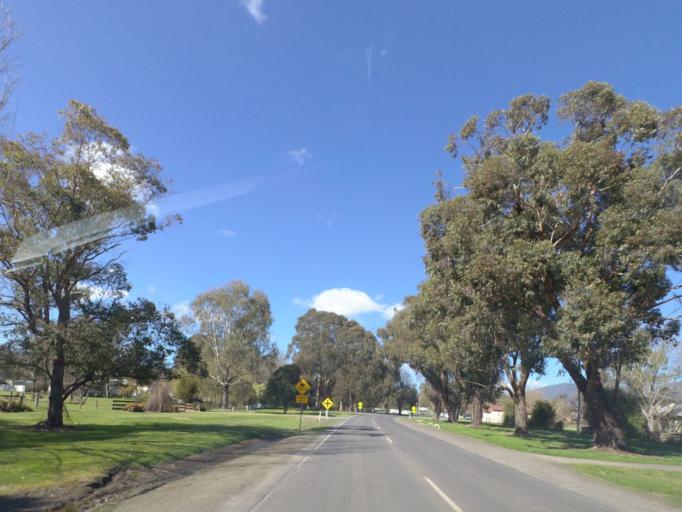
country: AU
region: Victoria
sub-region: Murrindindi
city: Alexandra
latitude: -37.2541
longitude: 145.7940
